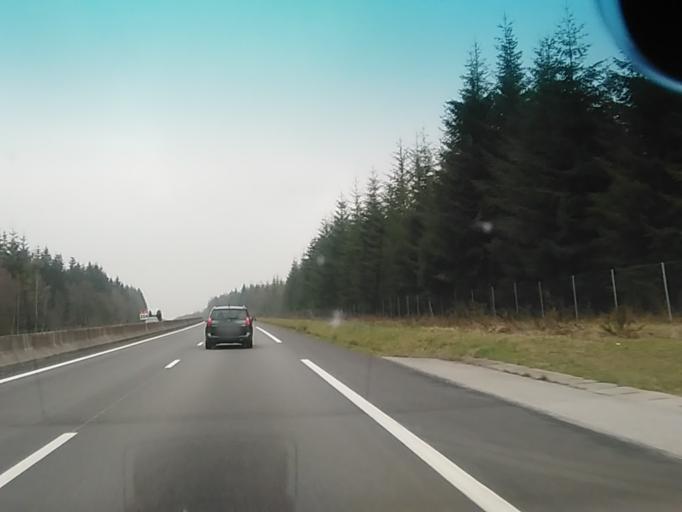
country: FR
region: Lower Normandy
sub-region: Departement de l'Orne
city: Gace
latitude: 48.7966
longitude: 0.3367
